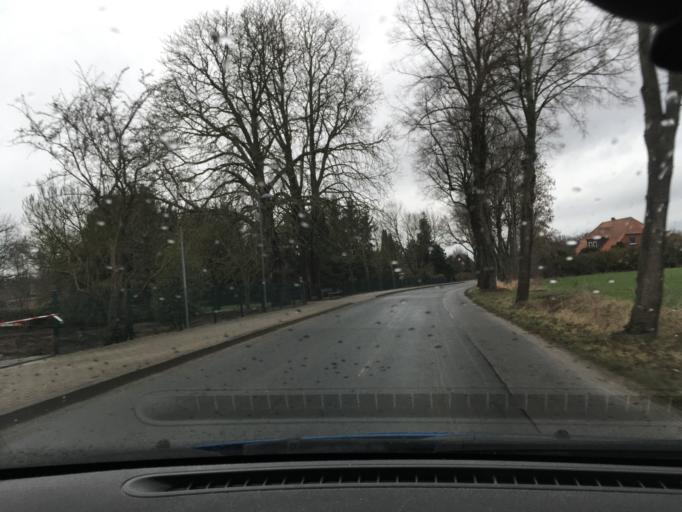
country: DE
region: Mecklenburg-Vorpommern
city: Nostorf
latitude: 53.3497
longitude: 10.6502
